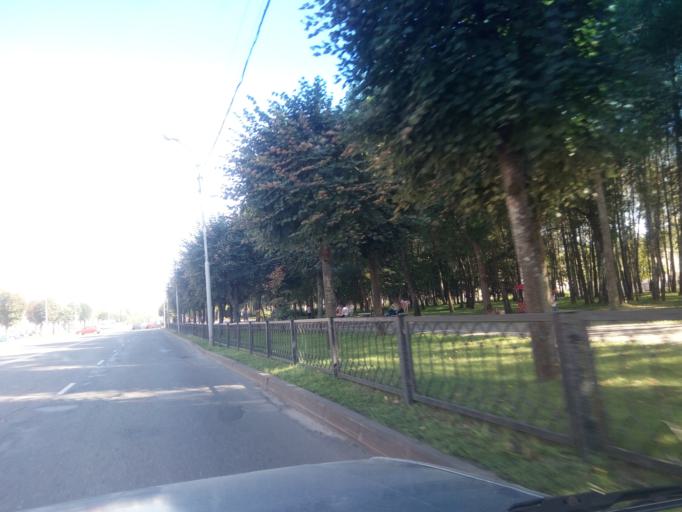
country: BY
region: Vitebsk
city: Navapolatsk
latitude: 55.5293
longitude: 28.6662
